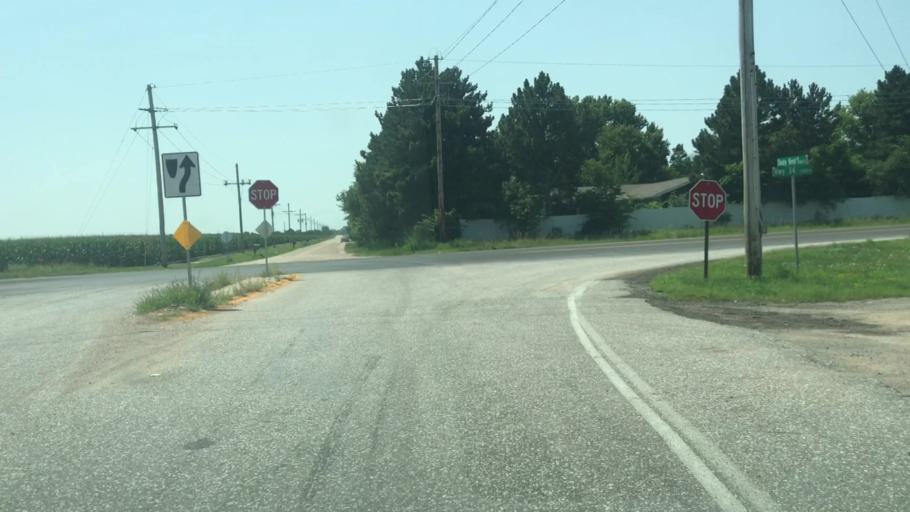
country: US
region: Nebraska
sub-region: Hall County
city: Grand Island
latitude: 40.8872
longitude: -98.3017
